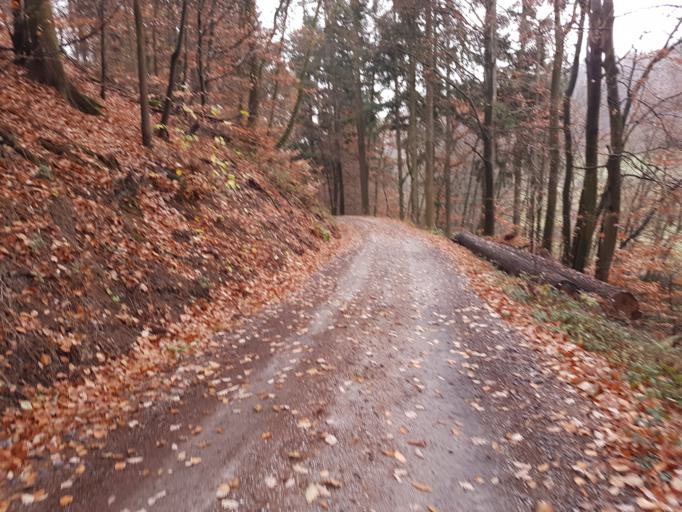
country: DE
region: Hesse
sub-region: Regierungsbezirk Darmstadt
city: Kiedrich
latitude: 50.0535
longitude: 8.0401
